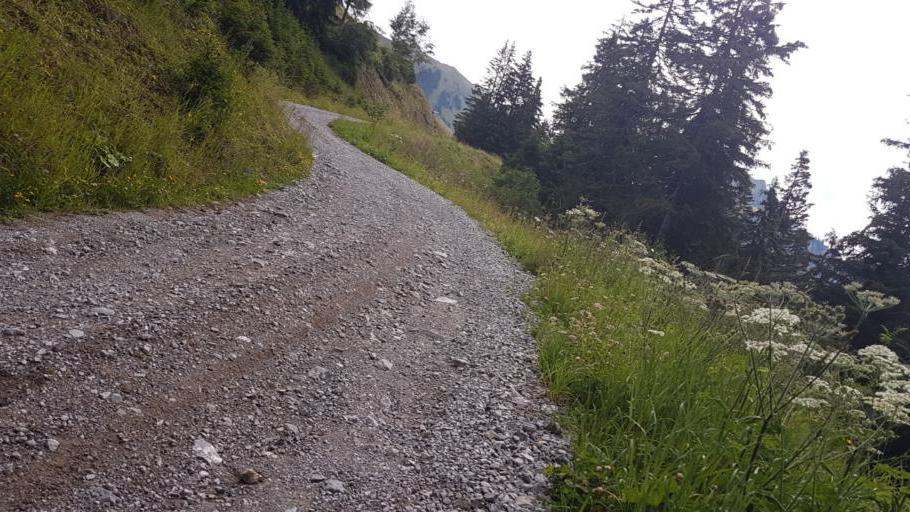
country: CH
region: Bern
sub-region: Obersimmental-Saanen District
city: Boltigen
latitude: 46.6919
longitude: 7.4356
